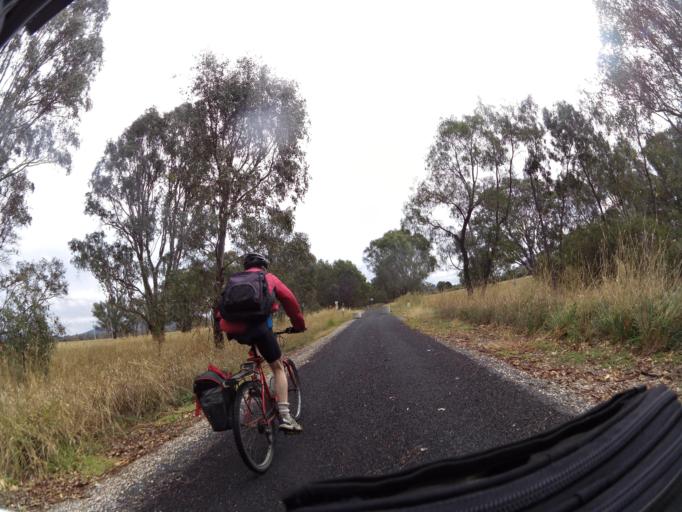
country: AU
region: New South Wales
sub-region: Albury Municipality
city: East Albury
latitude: -36.1404
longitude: 146.9824
